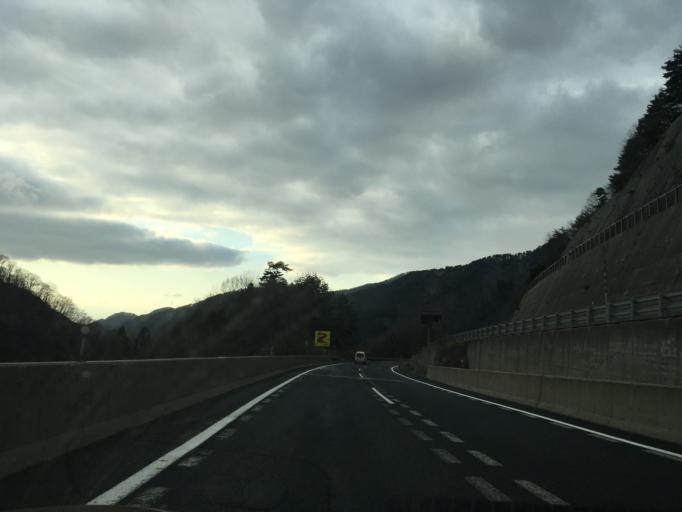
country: JP
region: Yamagata
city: Yamagata-shi
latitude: 38.2381
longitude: 140.4077
